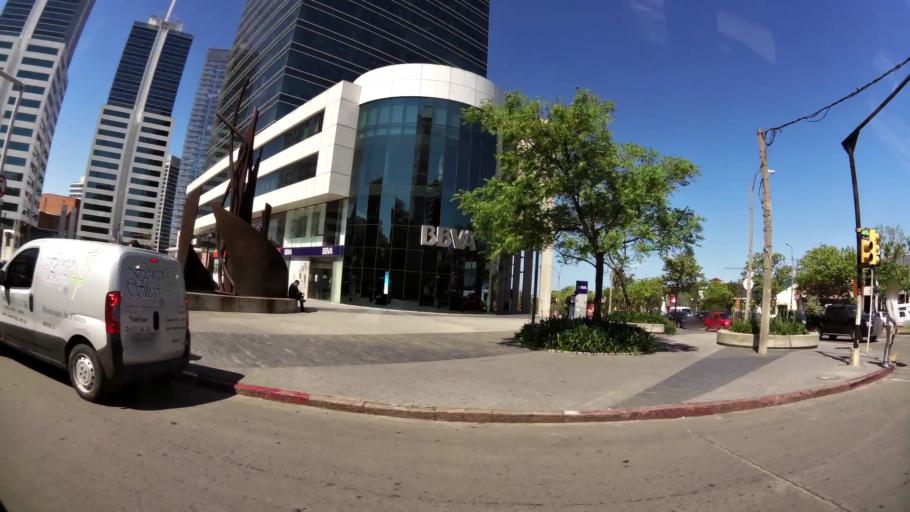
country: UY
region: Montevideo
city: Montevideo
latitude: -34.9055
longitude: -56.1368
